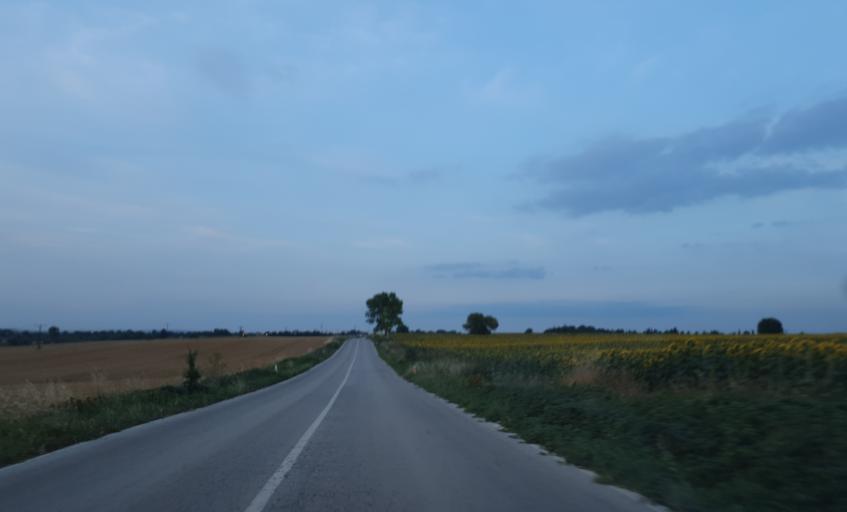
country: TR
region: Tekirdag
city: Beyazkoy
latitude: 41.4032
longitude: 27.6420
